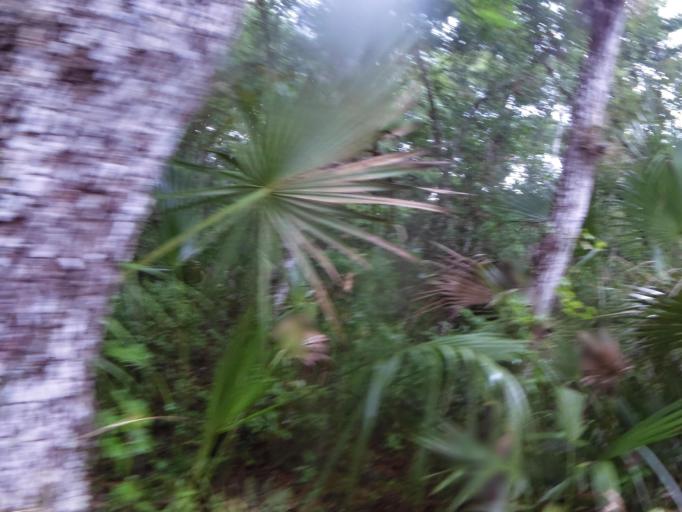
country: US
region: Florida
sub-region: Putnam County
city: Palatka
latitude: 29.6758
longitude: -81.7550
